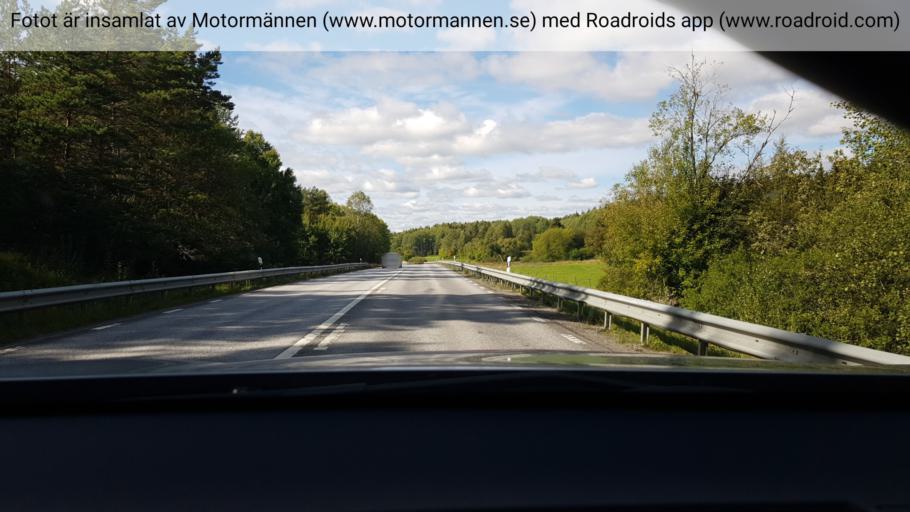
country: SE
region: Stockholm
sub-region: Vaxholms Kommun
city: Resaro
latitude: 59.4242
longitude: 18.2800
